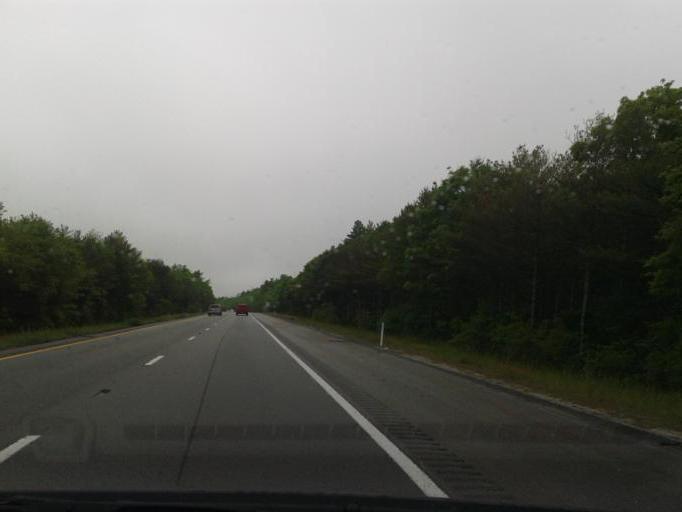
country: US
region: Massachusetts
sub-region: Plymouth County
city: Marion Center
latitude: 41.7219
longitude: -70.7793
